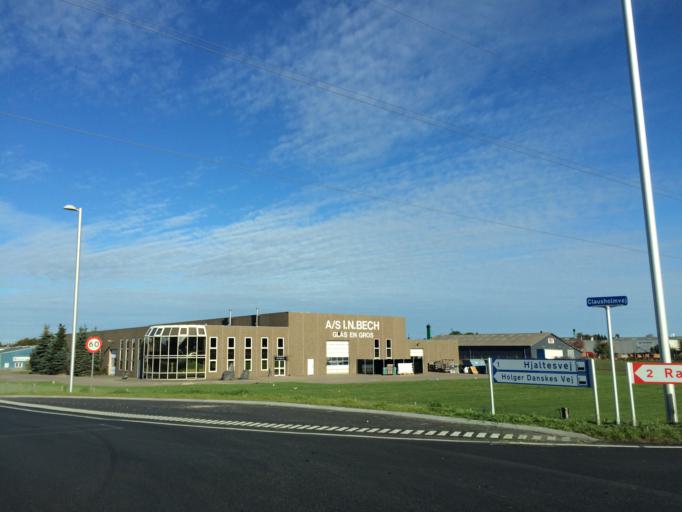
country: DK
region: Central Jutland
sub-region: Randers Kommune
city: Randers
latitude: 56.4395
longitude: 10.0725
